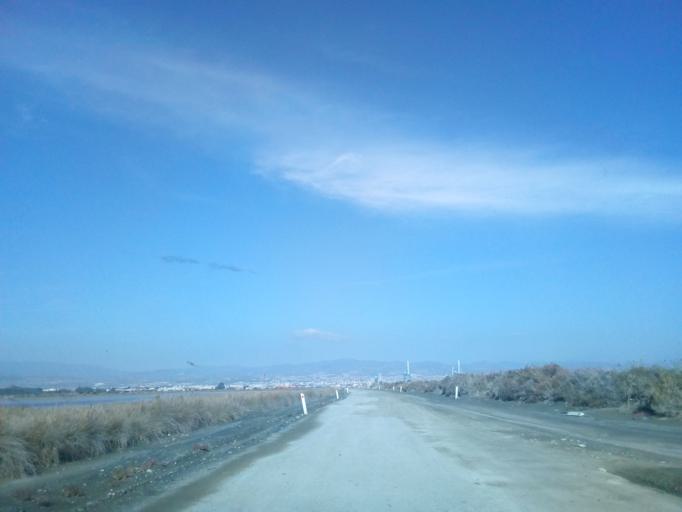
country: CY
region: Limassol
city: Limassol
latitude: 34.6280
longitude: 33.0064
